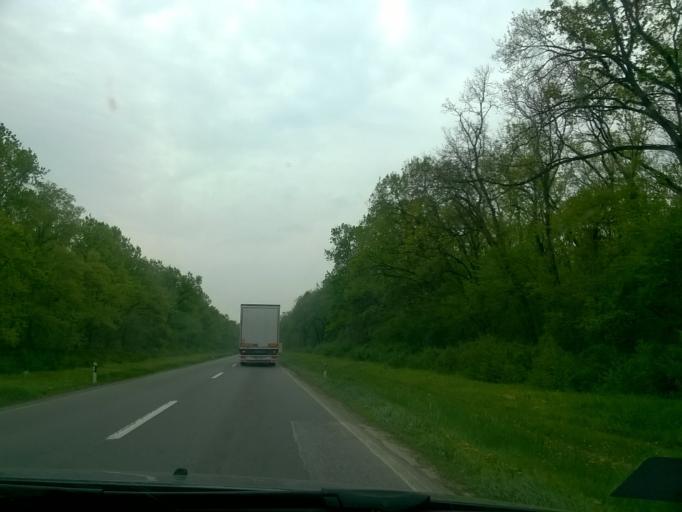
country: RS
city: Hrtkovci
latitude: 44.9003
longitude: 19.7643
